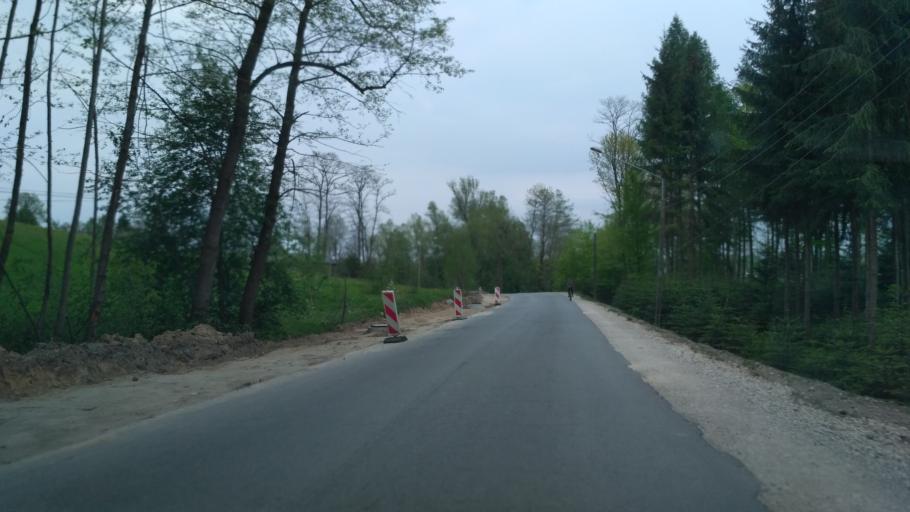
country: PL
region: Lesser Poland Voivodeship
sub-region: Powiat tarnowski
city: Skrzyszow
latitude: 49.9878
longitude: 21.0628
